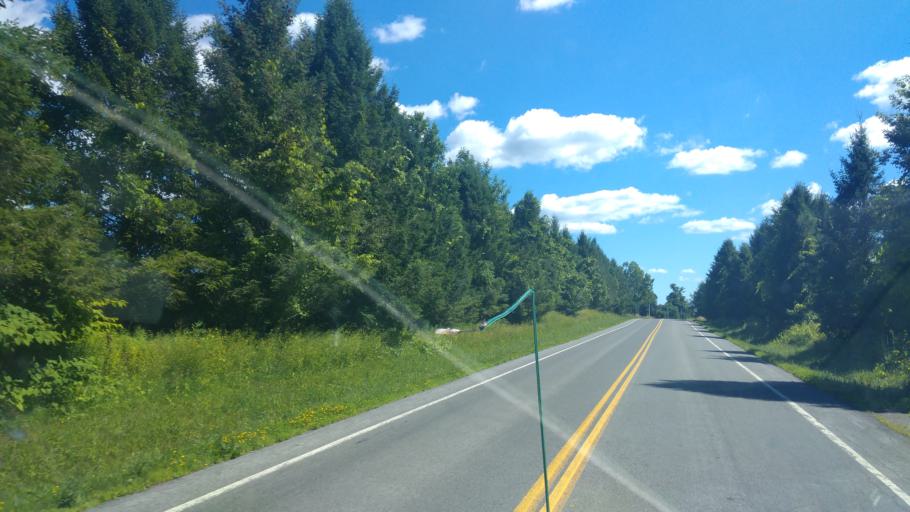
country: US
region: New York
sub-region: Wayne County
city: Sodus
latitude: 43.1626
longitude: -77.0124
